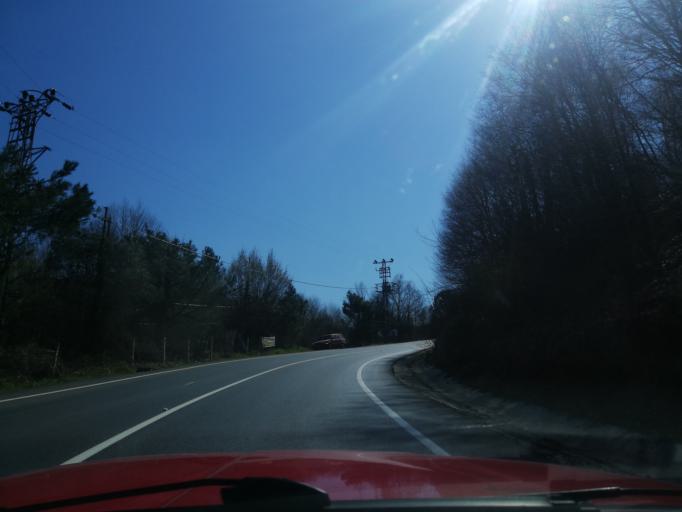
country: TR
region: Istanbul
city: Mahmut Sevket Pasa
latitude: 41.1244
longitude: 29.1563
